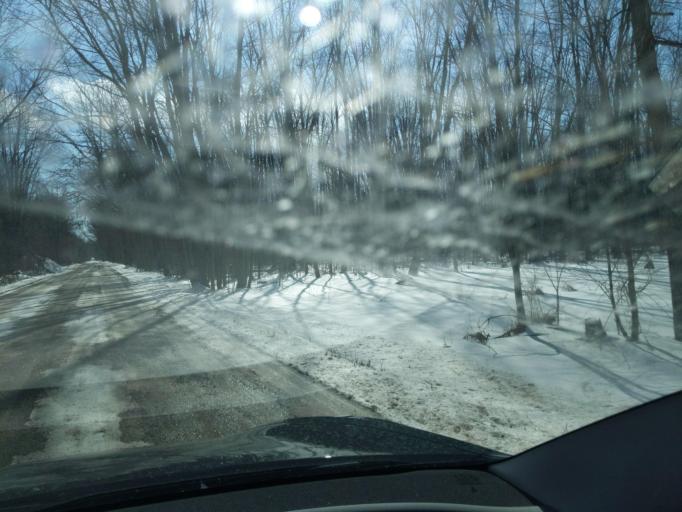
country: US
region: Michigan
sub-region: Livingston County
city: Fowlerville
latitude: 42.5490
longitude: -84.0884
